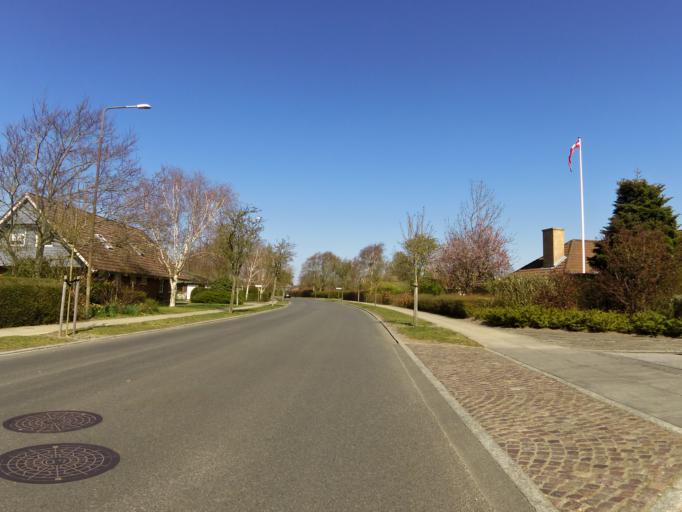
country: DK
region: South Denmark
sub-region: Esbjerg Kommune
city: Ribe
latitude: 55.3448
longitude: 8.7795
